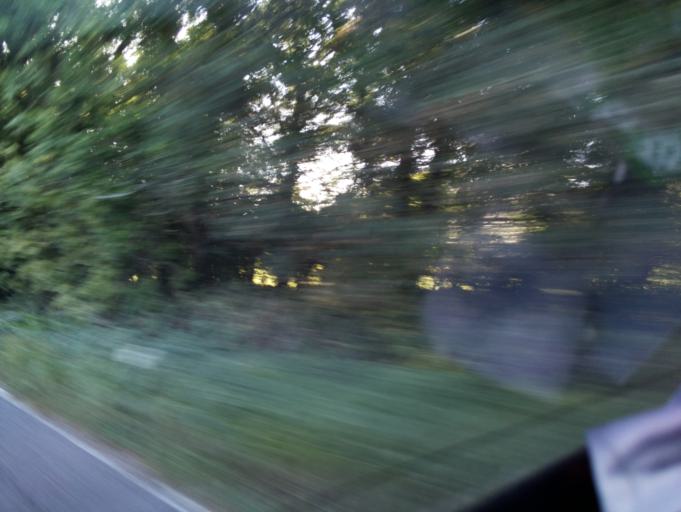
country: GB
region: England
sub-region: Hampshire
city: Bishops Waltham
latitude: 50.9399
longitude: -1.2301
